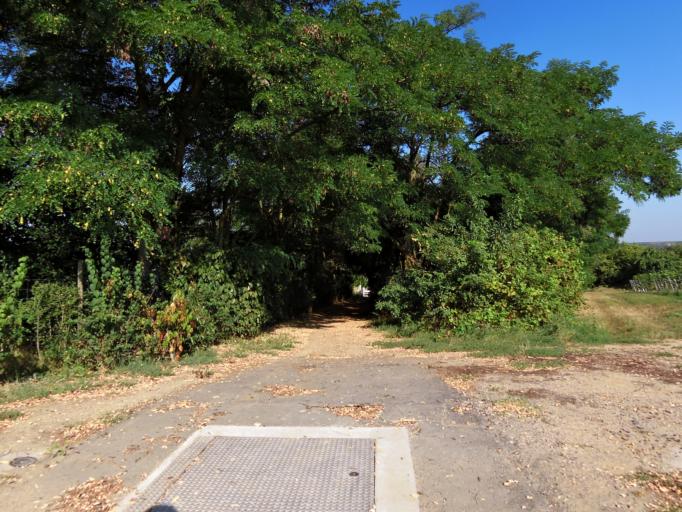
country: DE
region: Rheinland-Pfalz
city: Freinsheim
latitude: 49.5008
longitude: 8.2159
